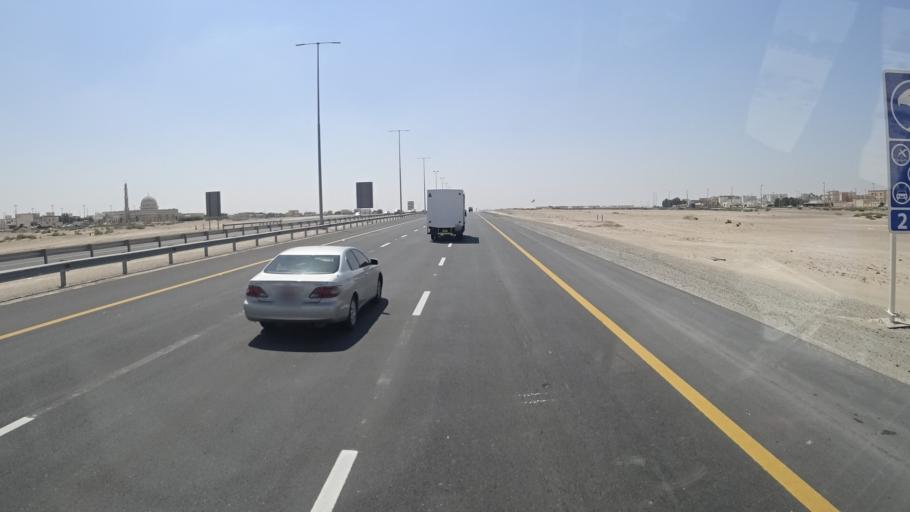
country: AE
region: Abu Dhabi
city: Abu Dhabi
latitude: 24.3305
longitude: 54.6929
